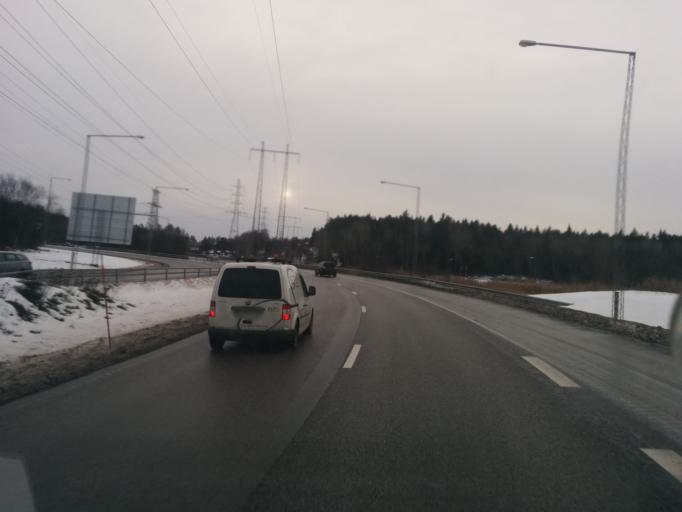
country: SE
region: Stockholm
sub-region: Sollentuna Kommun
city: Sollentuna
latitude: 59.4363
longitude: 17.9221
